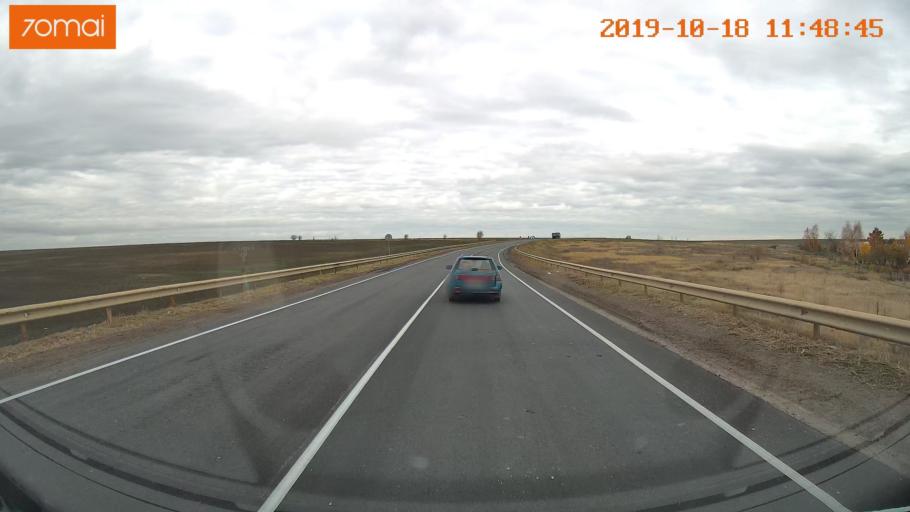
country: RU
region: Rjazan
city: Mikhaylov
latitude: 54.2413
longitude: 38.9853
